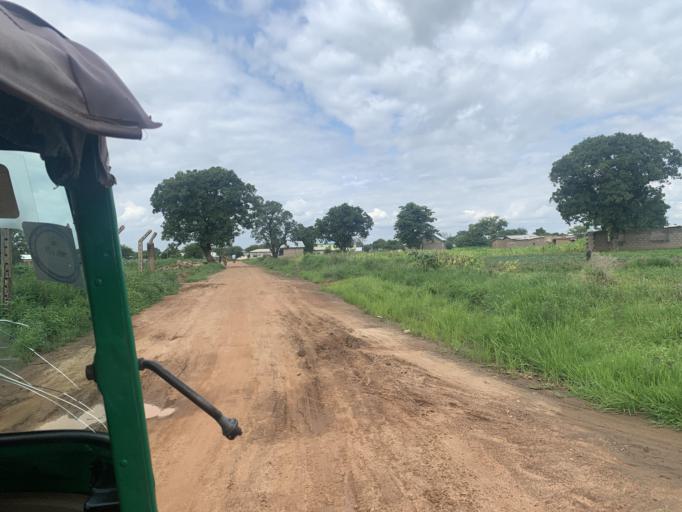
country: GH
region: Upper East
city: Navrongo
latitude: 10.8648
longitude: -1.0737
